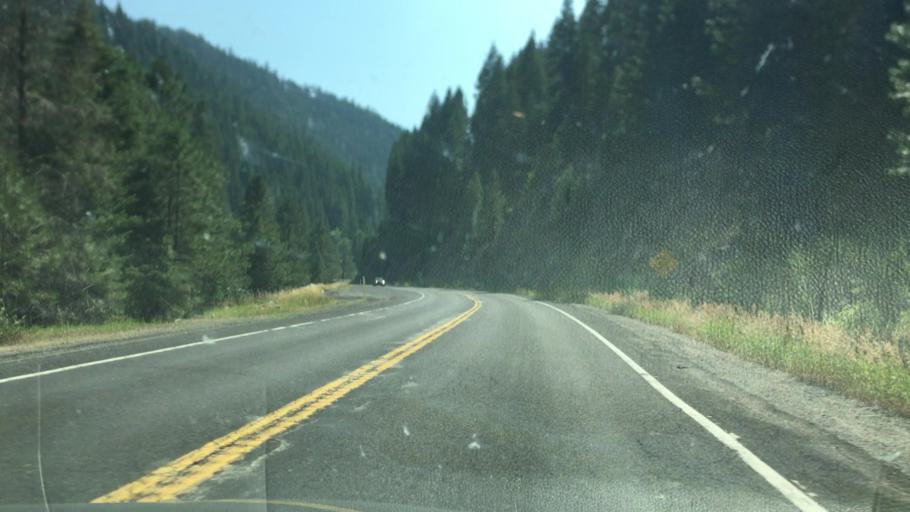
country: US
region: Idaho
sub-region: Valley County
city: Cascade
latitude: 44.2584
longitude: -116.0814
